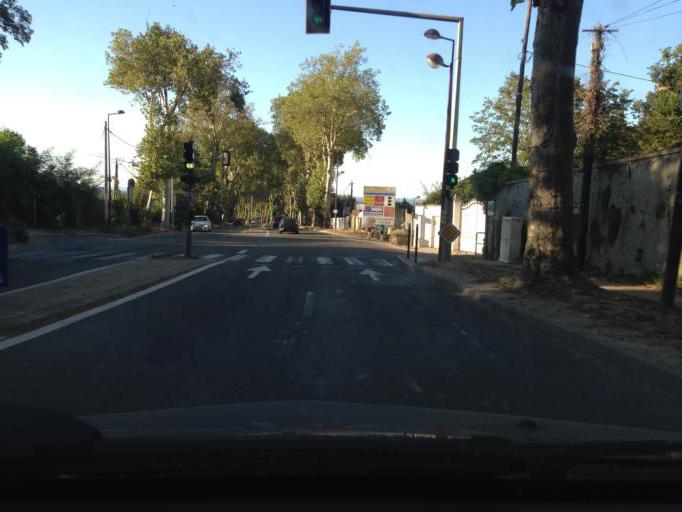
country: FR
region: Ile-de-France
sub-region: Departement des Yvelines
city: Louveciennes
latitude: 48.8659
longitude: 2.1129
